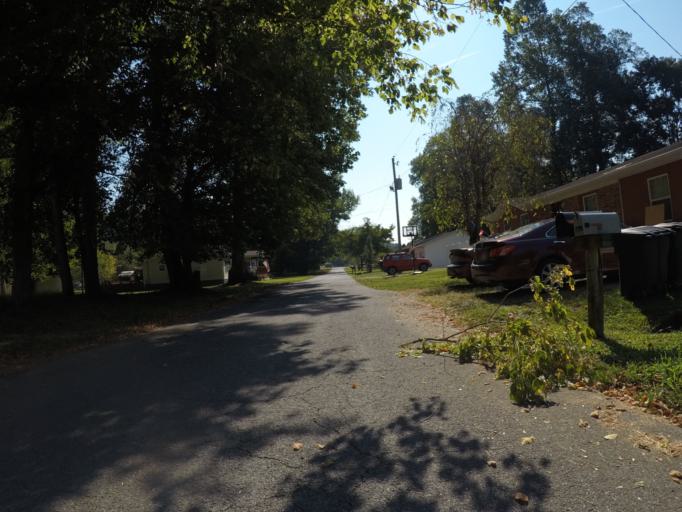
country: US
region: West Virginia
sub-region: Cabell County
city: Barboursville
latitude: 38.3746
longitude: -82.2795
